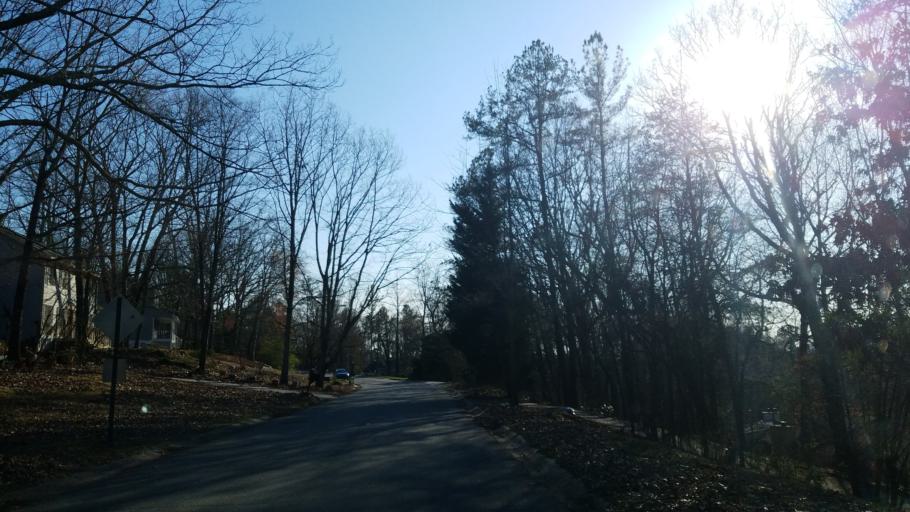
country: US
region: Georgia
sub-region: Cobb County
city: Marietta
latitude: 33.9981
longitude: -84.4934
